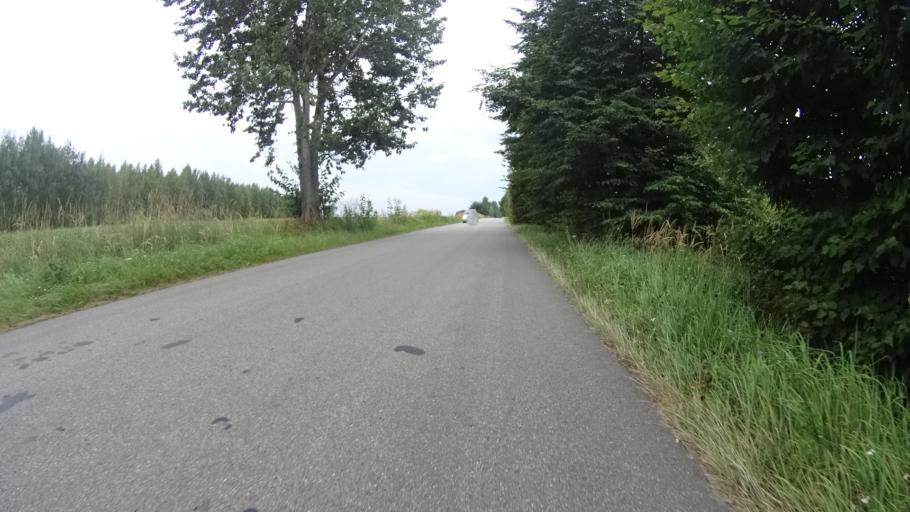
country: PL
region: Masovian Voivodeship
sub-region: Powiat grojecki
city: Goszczyn
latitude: 51.6830
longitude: 20.8609
